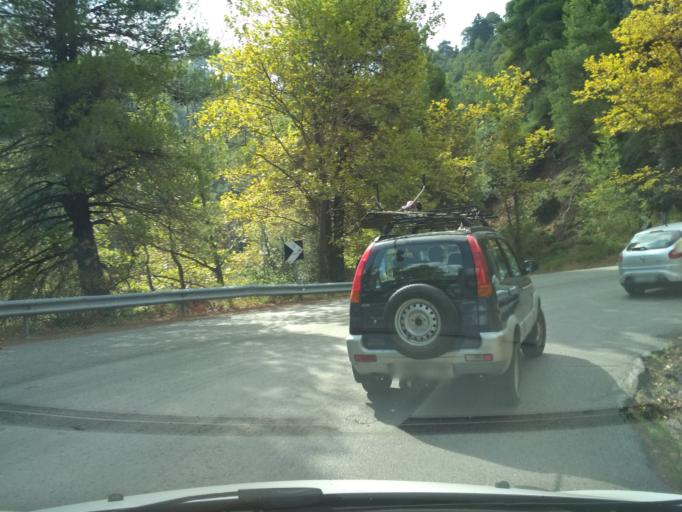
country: GR
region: Central Greece
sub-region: Nomos Evvoias
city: Politika
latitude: 38.6714
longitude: 23.5595
